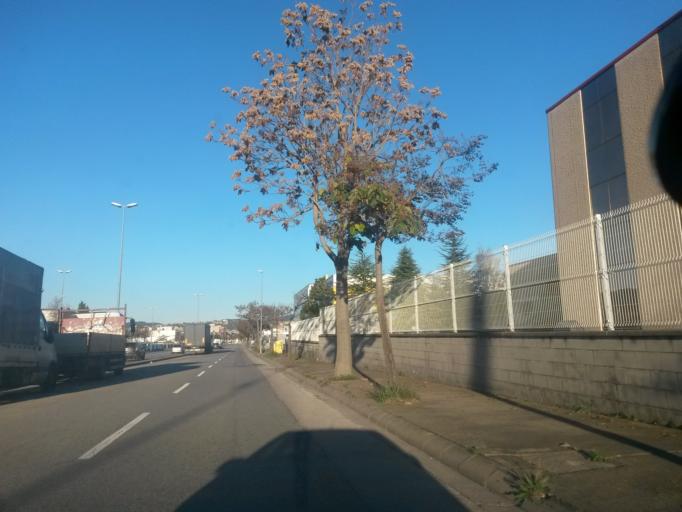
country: ES
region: Catalonia
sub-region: Provincia de Girona
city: Salt
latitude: 41.9614
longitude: 2.8045
